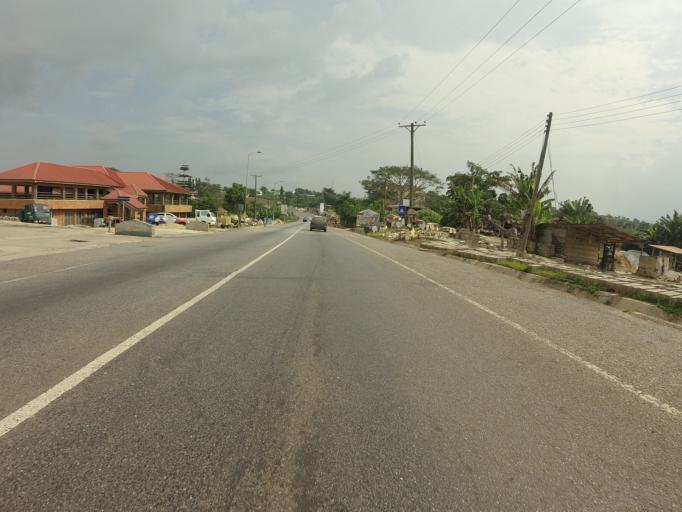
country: GH
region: Eastern
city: Aburi
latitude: 5.8095
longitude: -0.1846
